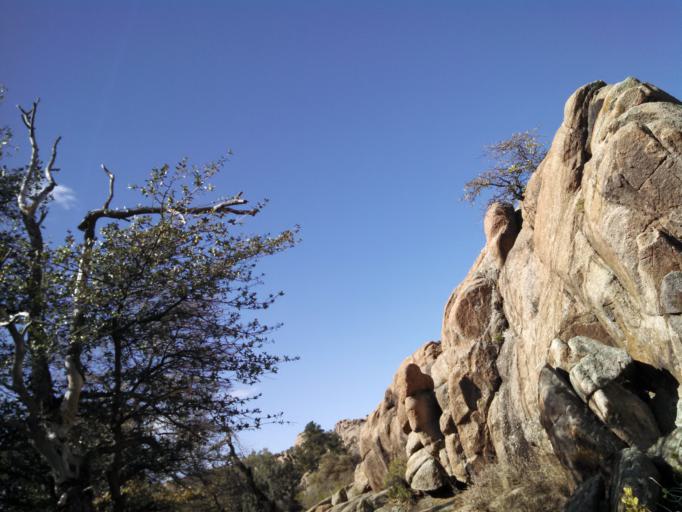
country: US
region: Arizona
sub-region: Yavapai County
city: Prescott
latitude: 34.5916
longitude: -112.4029
